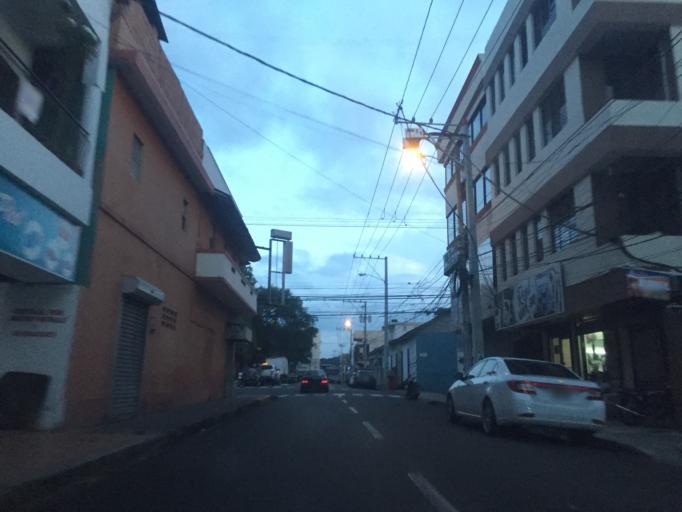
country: DO
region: Santiago
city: Santiago de los Caballeros
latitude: 19.4550
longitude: -70.7100
